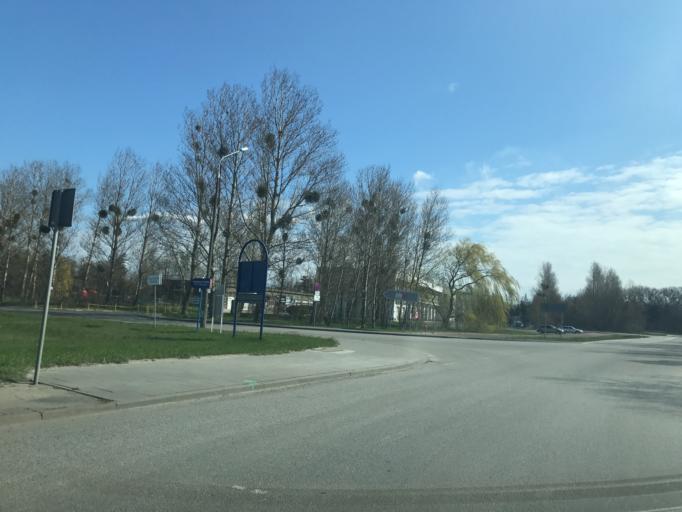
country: PL
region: Pomeranian Voivodeship
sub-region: Gdansk
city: Gdansk
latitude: 54.4026
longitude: 18.6834
